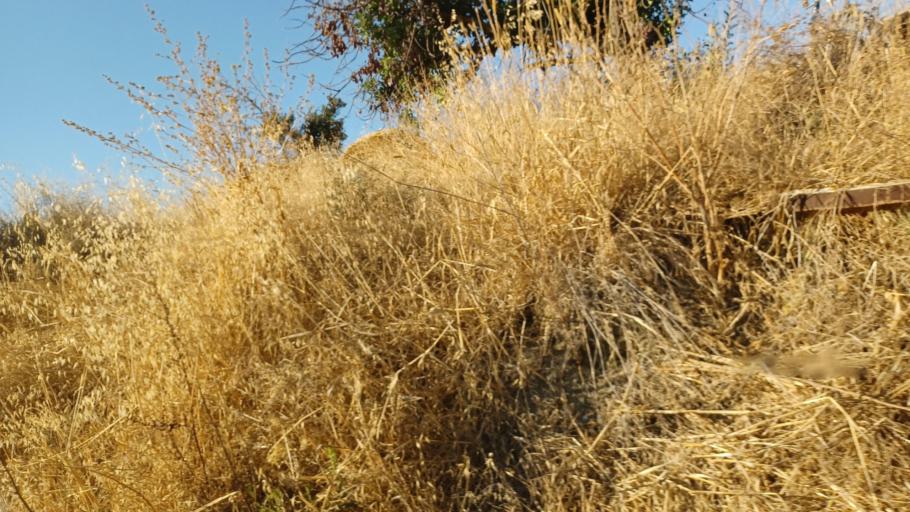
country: CY
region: Pafos
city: Polis
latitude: 35.0018
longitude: 32.4639
